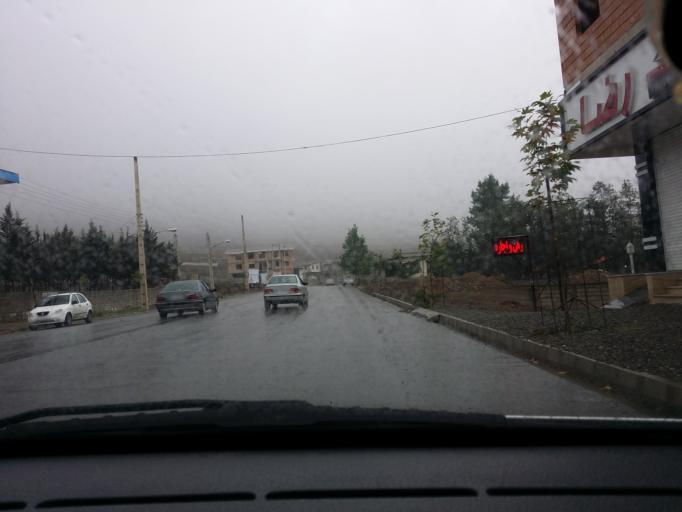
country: IR
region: Mazandaran
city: Chalus
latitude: 36.5216
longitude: 51.2351
